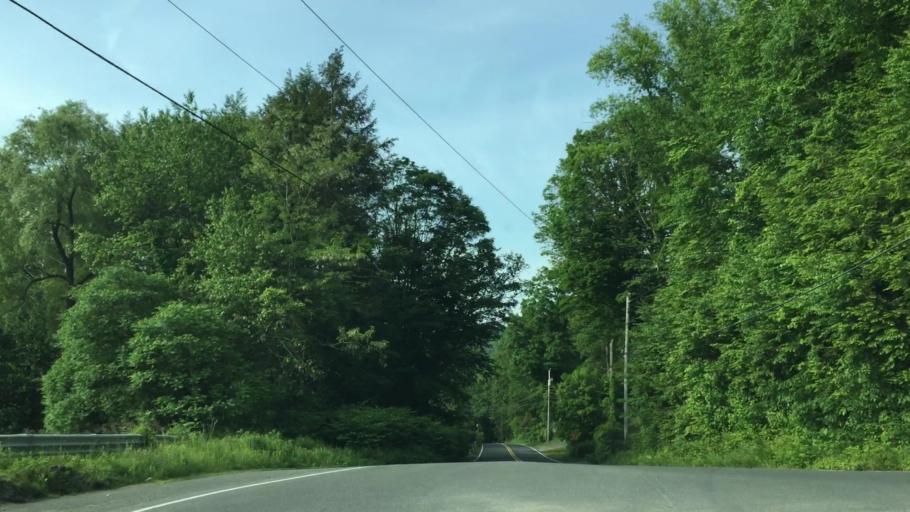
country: US
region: Massachusetts
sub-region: Hampshire County
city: Westhampton
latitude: 42.2449
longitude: -72.8797
